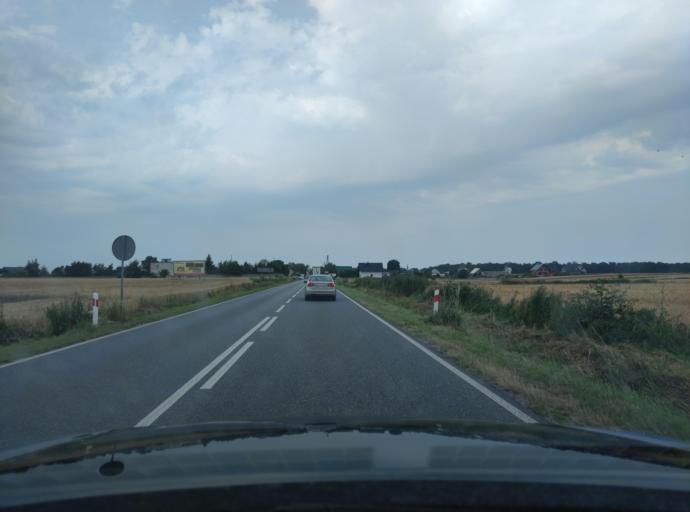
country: PL
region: Opole Voivodeship
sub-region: Powiat strzelecki
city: Strzelce Opolskie
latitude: 50.4955
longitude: 18.2890
